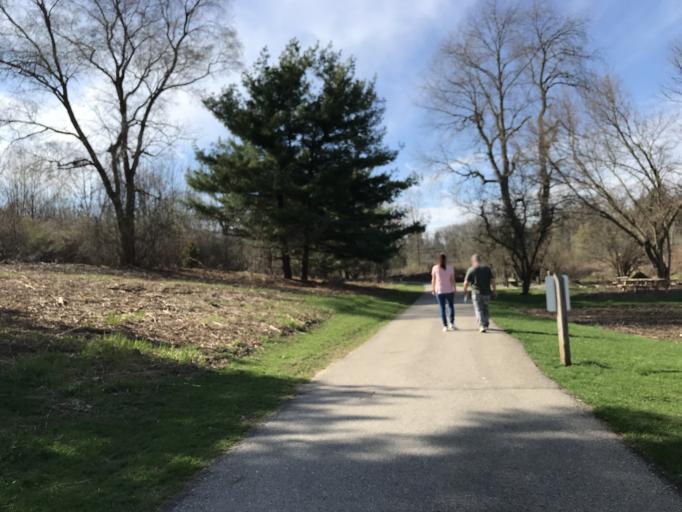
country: US
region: Michigan
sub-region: Washtenaw County
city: Ann Arbor
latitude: 42.2565
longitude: -83.7041
